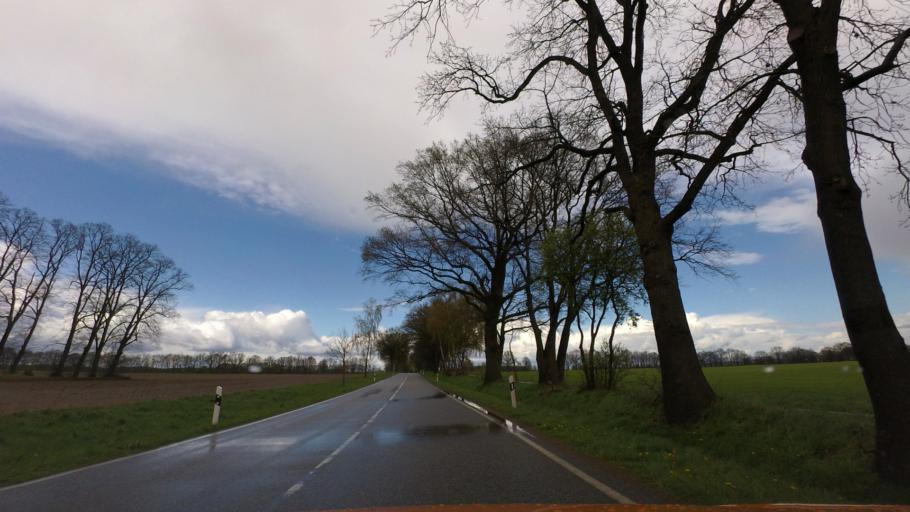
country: DE
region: Mecklenburg-Vorpommern
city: Nostorf
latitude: 53.4007
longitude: 10.6373
